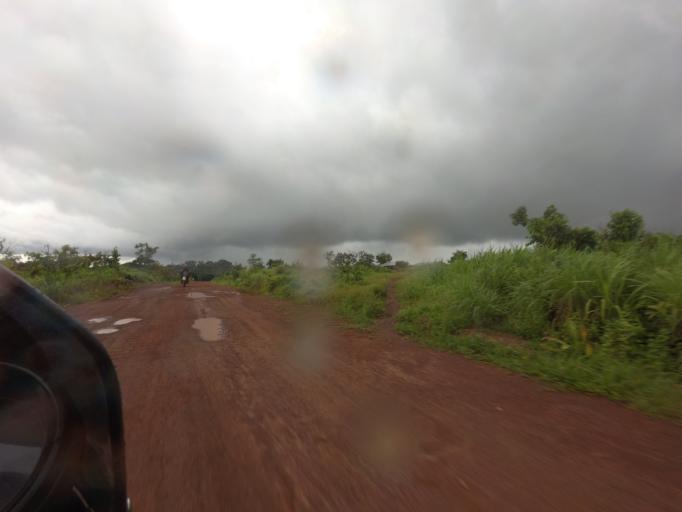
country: SL
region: Northern Province
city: Kukuna
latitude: 9.2628
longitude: -12.7306
